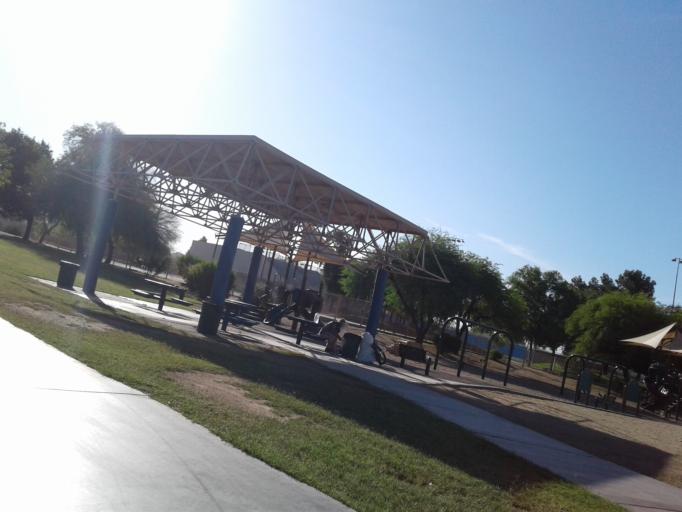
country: US
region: Arizona
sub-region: Maricopa County
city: Glendale
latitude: 33.5775
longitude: -112.1117
